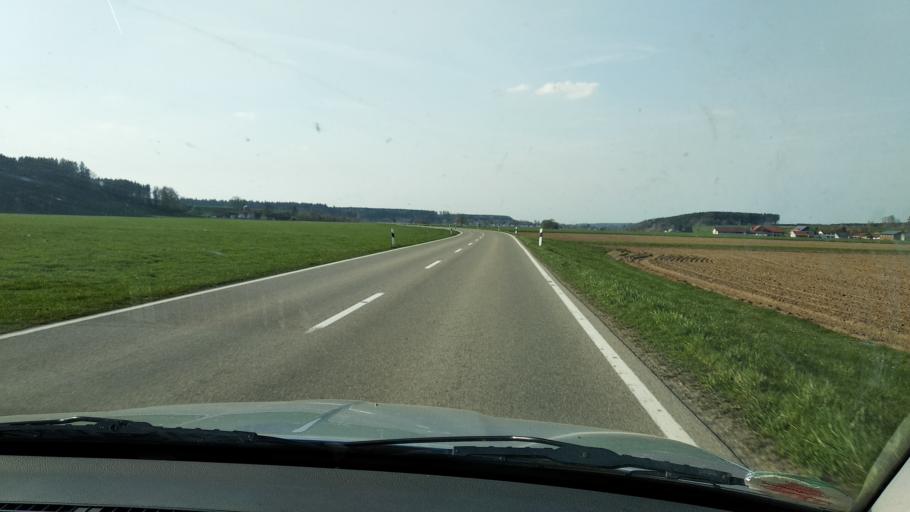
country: DE
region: Bavaria
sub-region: Swabia
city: Legau
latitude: 47.8728
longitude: 10.1242
